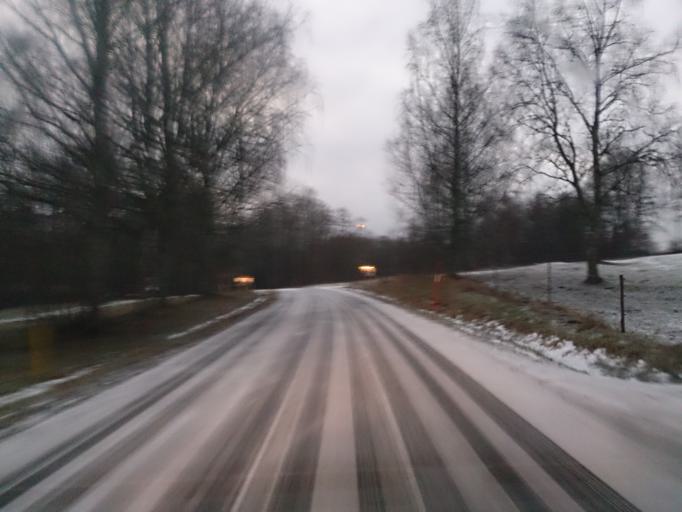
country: SE
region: OEstergoetland
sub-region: Atvidabergs Kommun
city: Atvidaberg
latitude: 58.2784
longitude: 16.1802
